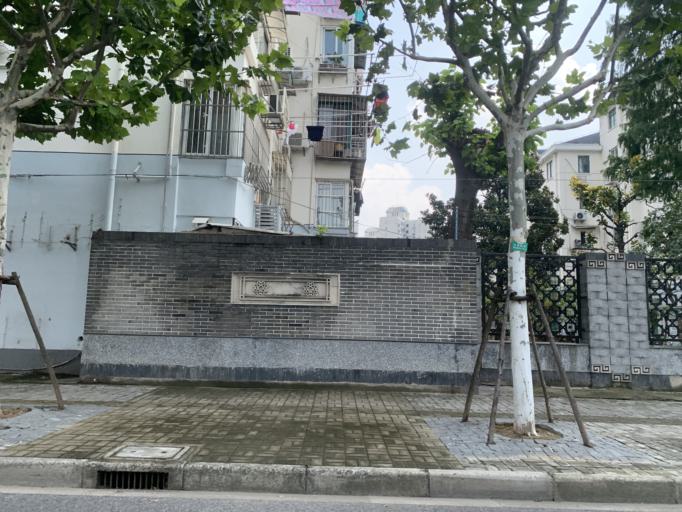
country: CN
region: Shanghai Shi
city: Luwan
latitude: 31.1833
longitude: 121.4924
